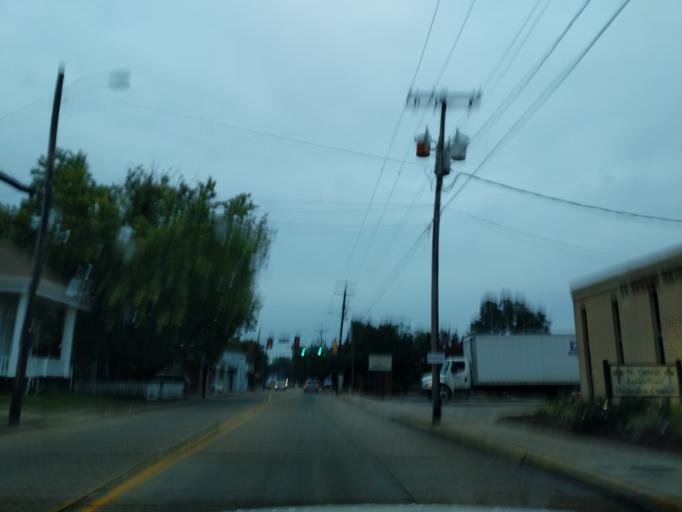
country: US
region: Mississippi
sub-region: Warren County
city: Vicksburg
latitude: 32.3345
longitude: -90.8873
